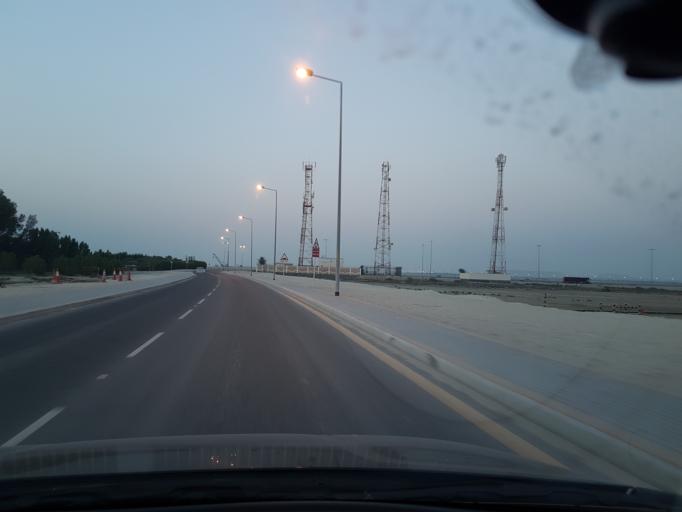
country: BH
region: Central Governorate
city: Dar Kulayb
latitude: 25.9937
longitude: 50.4674
